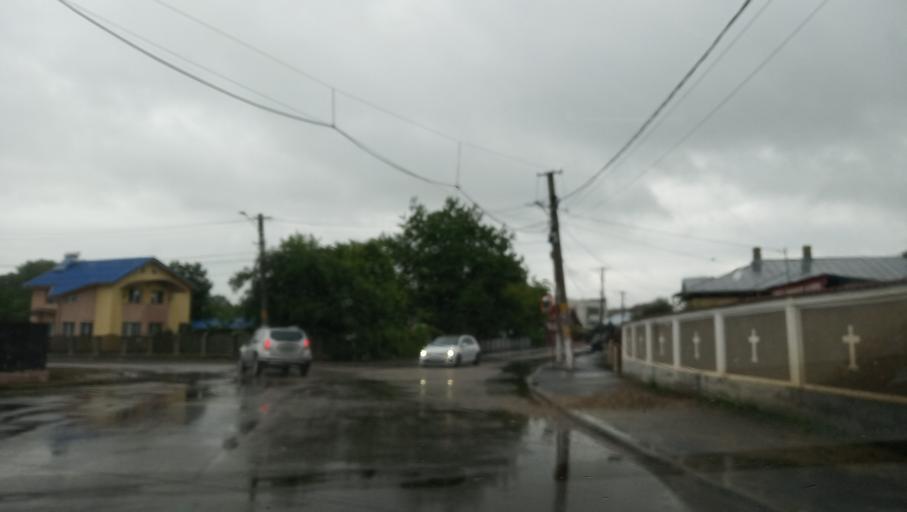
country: RO
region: Dambovita
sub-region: Oras Gaesti
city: Gaesti
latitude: 44.7162
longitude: 25.3234
